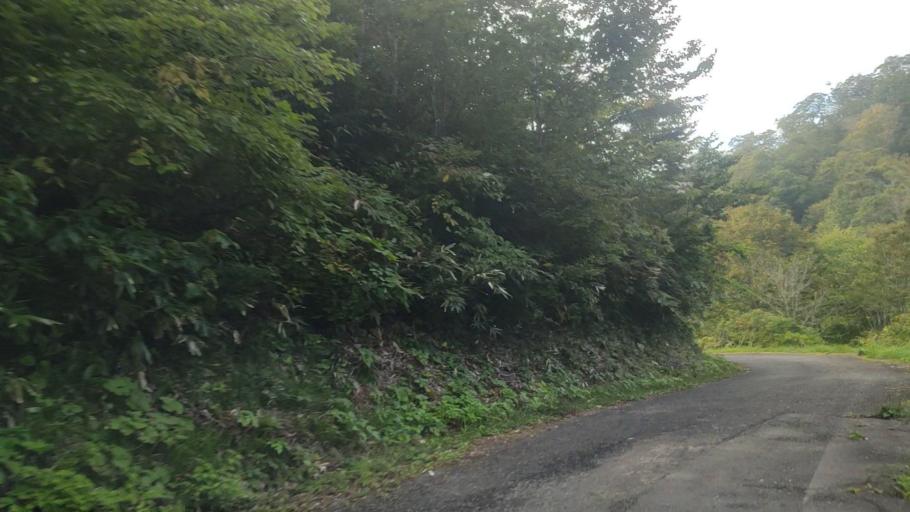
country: JP
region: Toyama
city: Yatsuomachi-higashikumisaka
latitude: 36.3470
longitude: 137.0657
